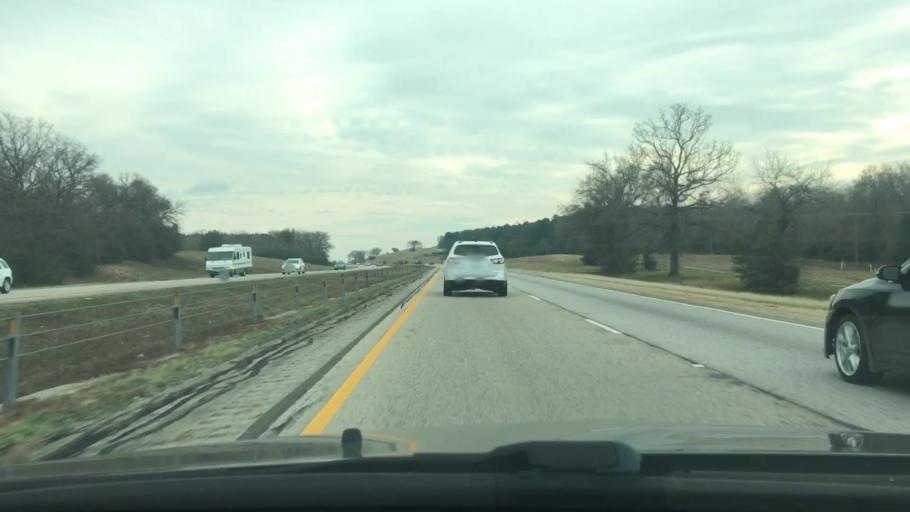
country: US
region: Texas
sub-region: Leon County
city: Centerville
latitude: 31.2970
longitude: -95.9989
